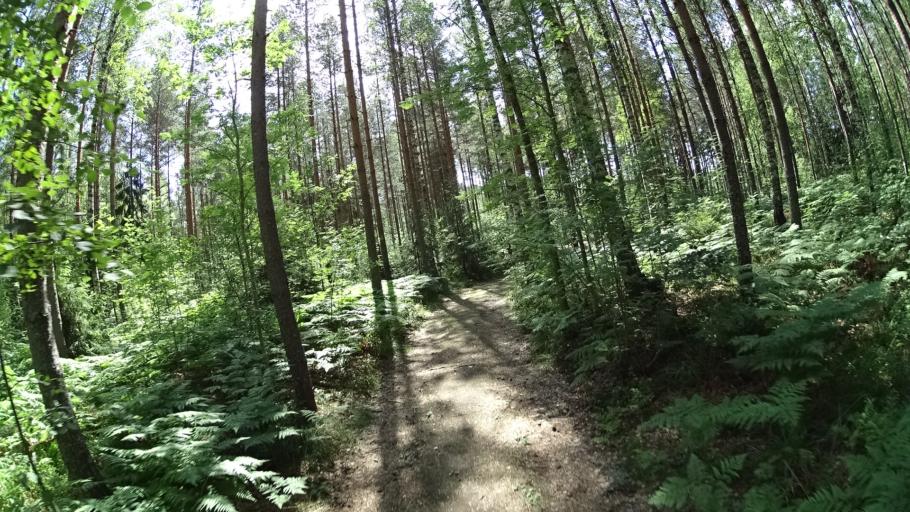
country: FI
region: Haeme
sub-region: Forssa
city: Tammela
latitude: 60.7716
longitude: 23.8677
